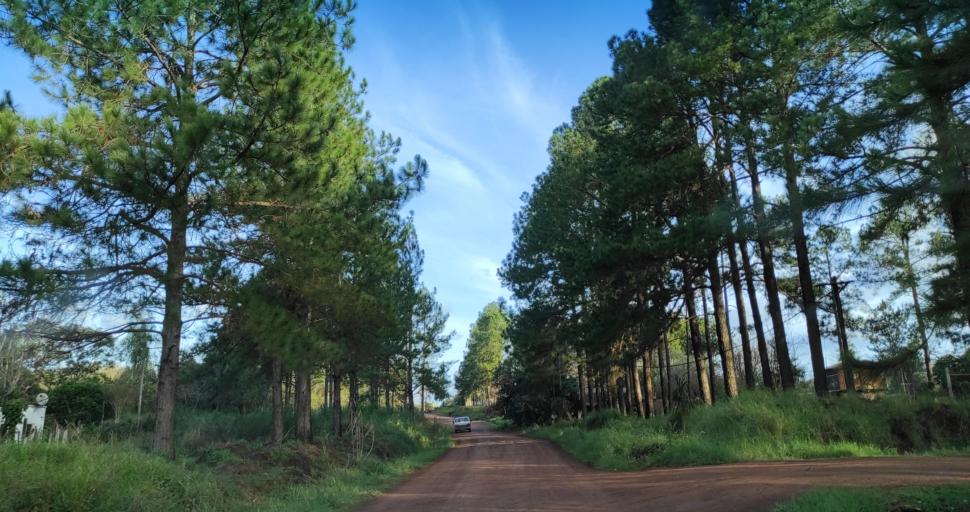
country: AR
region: Misiones
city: Garupa
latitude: -27.5111
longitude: -55.8547
